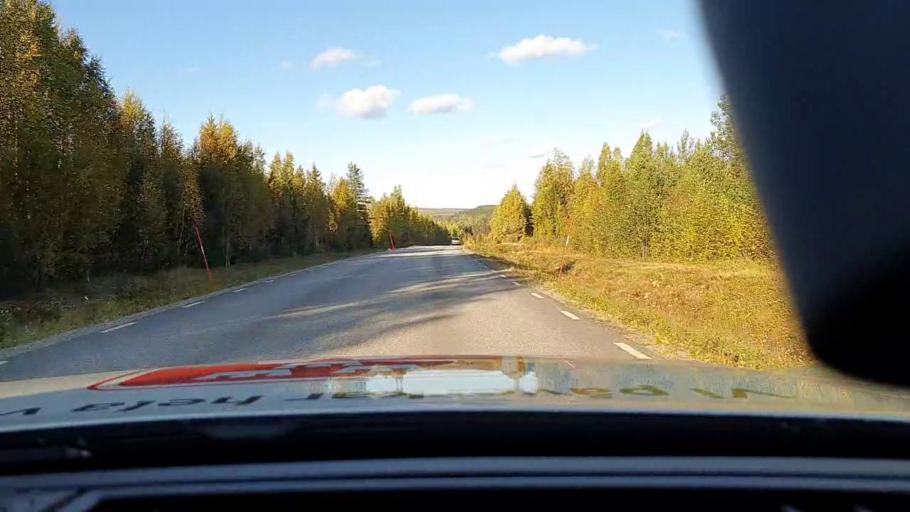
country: SE
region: Norrbotten
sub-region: Pitea Kommun
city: Norrfjarden
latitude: 65.5037
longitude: 21.4783
